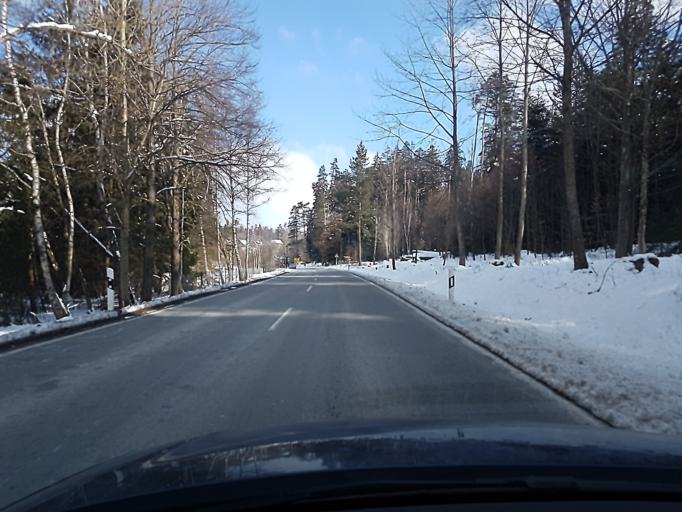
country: DE
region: Baden-Wuerttemberg
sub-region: Freiburg Region
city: Konigsfeld im Schwarzwald
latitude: 48.1381
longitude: 8.4244
